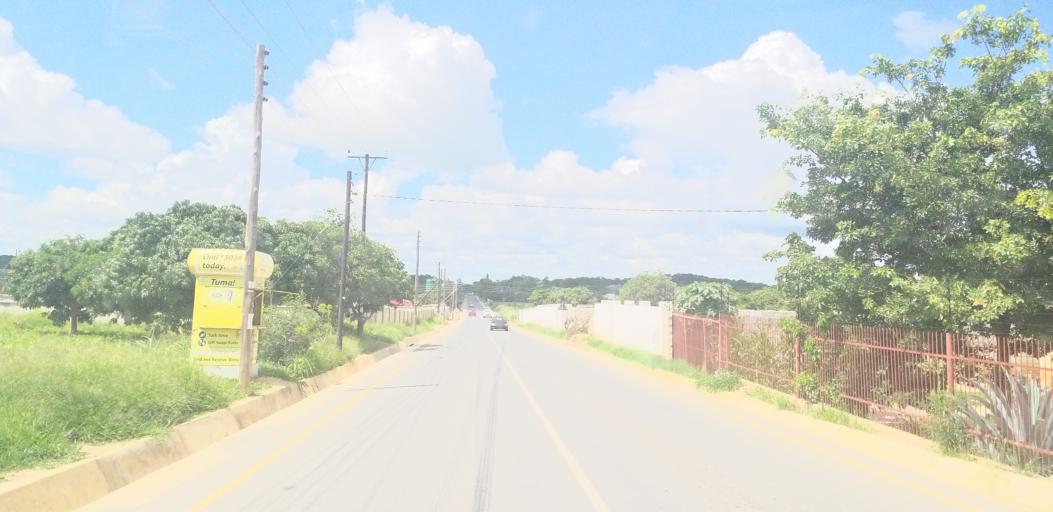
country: ZM
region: Lusaka
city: Lusaka
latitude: -15.3402
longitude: 28.3285
